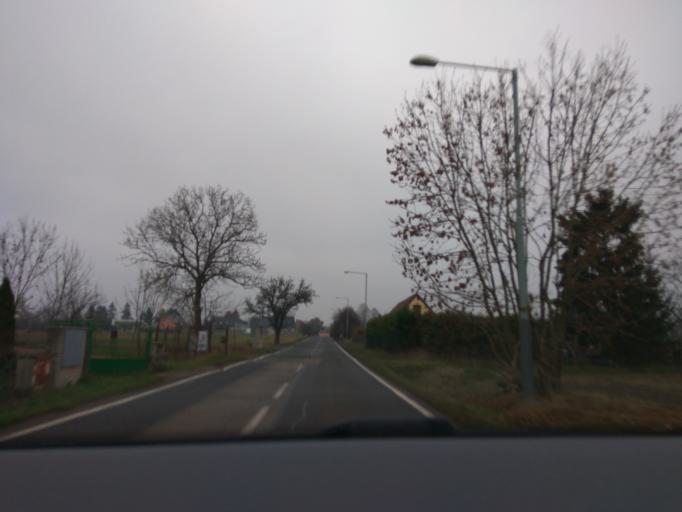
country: CZ
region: Central Bohemia
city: Hovorcovice
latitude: 50.1680
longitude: 14.5224
